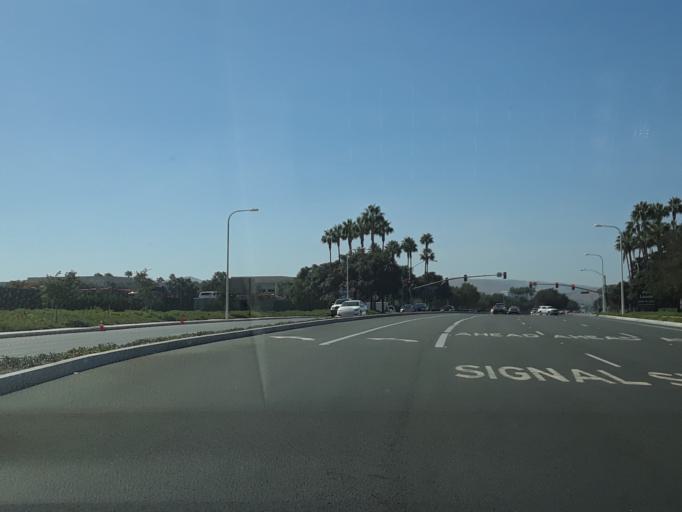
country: US
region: California
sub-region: Orange County
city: Irvine
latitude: 33.6746
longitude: -117.7615
